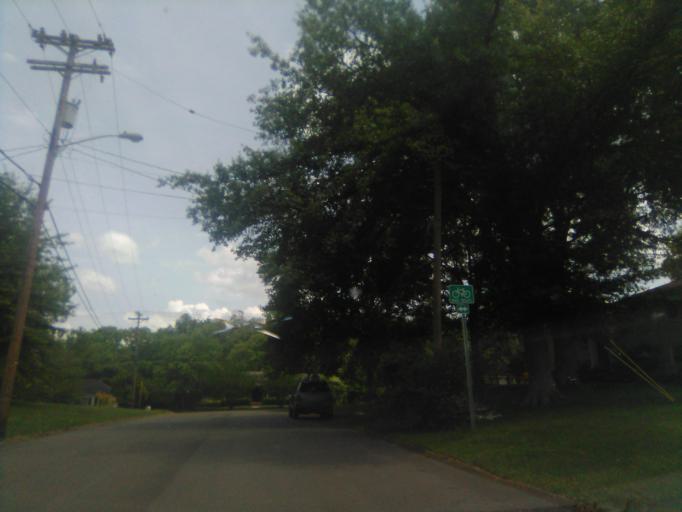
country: US
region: Tennessee
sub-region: Davidson County
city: Belle Meade
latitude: 36.0917
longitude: -86.8804
